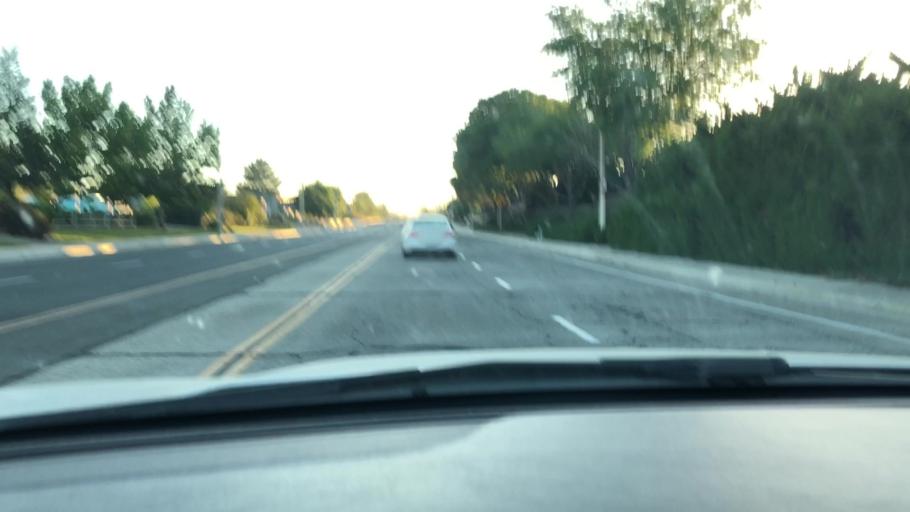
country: US
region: California
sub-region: Los Angeles County
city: Quartz Hill
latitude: 34.6822
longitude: -118.1866
